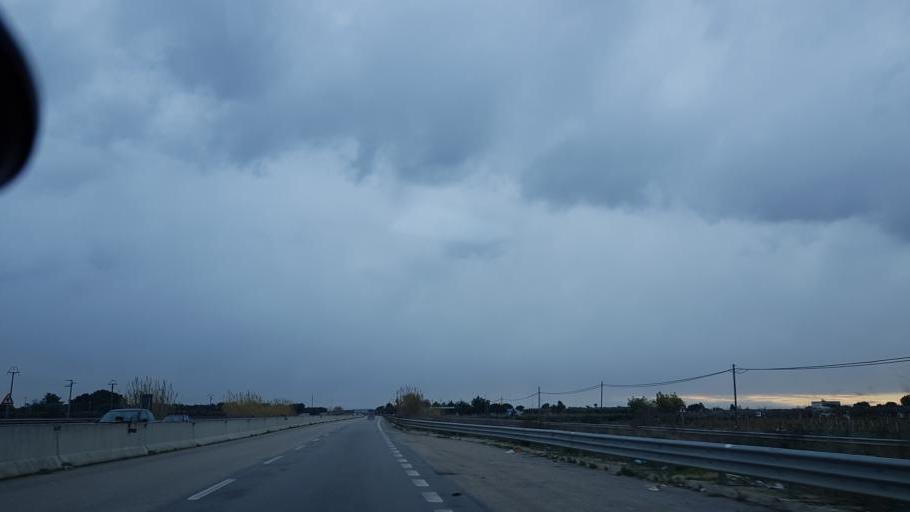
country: IT
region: Apulia
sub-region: Provincia di Brindisi
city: Brindisi
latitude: 40.5994
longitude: 17.8741
